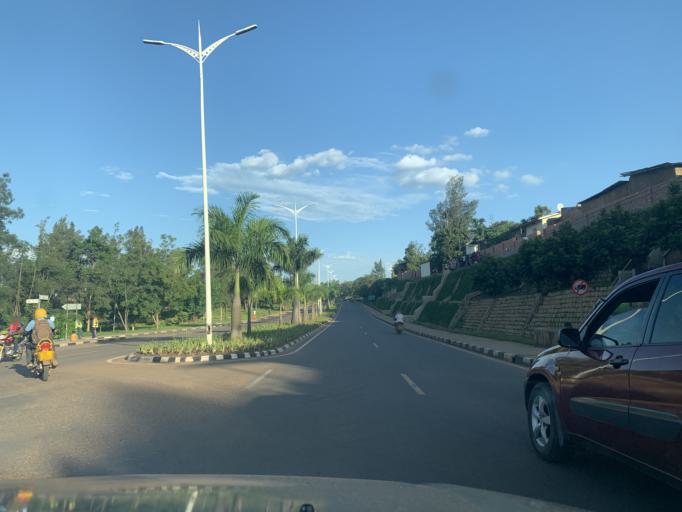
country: RW
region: Kigali
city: Kigali
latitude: -1.9628
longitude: 30.1251
